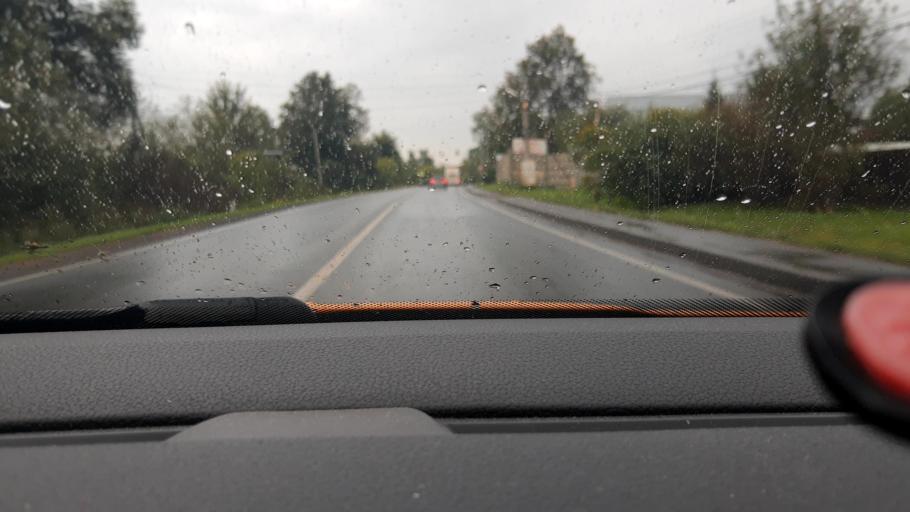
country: RU
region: Moskovskaya
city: Obukhovo
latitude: 55.8150
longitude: 38.2568
